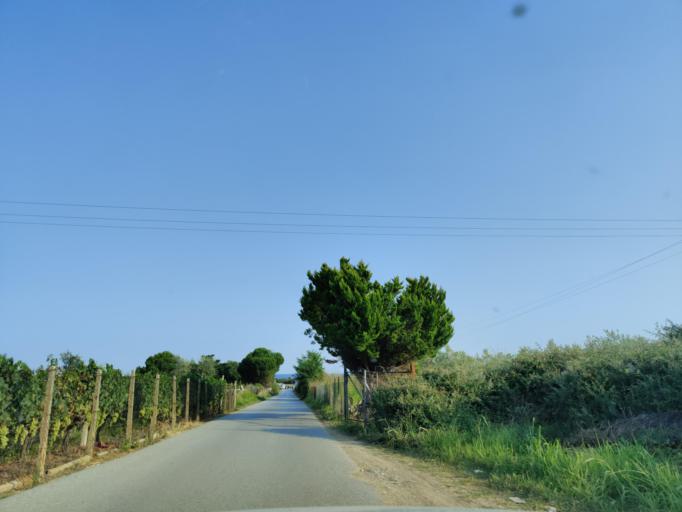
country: GR
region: East Macedonia and Thrace
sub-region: Nomos Kavalas
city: Nea Peramos
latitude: 40.8160
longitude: 24.2871
